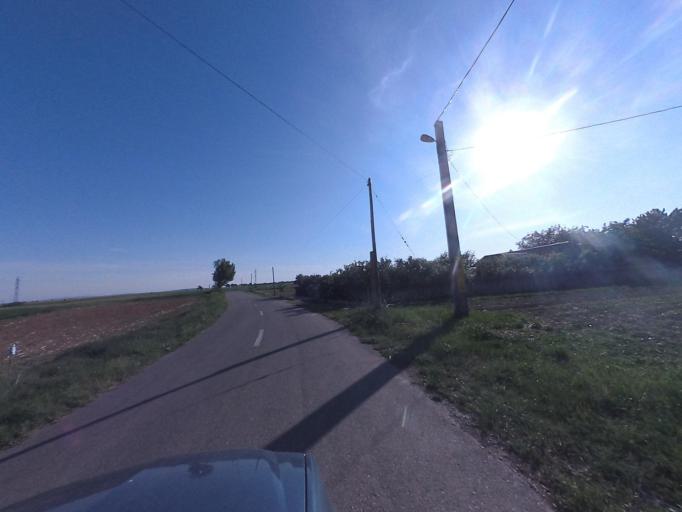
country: RO
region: Neamt
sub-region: Comuna Cordun
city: Pildesti
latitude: 46.9790
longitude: 26.8031
